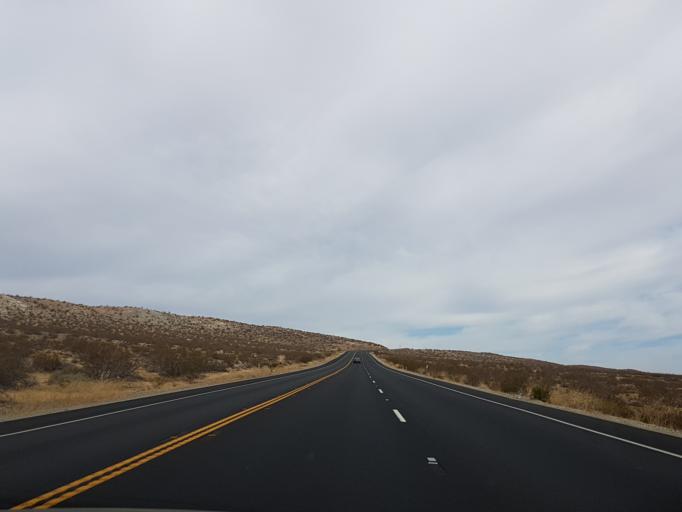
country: US
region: California
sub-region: Kern County
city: Ridgecrest
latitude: 35.4468
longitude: -117.6607
